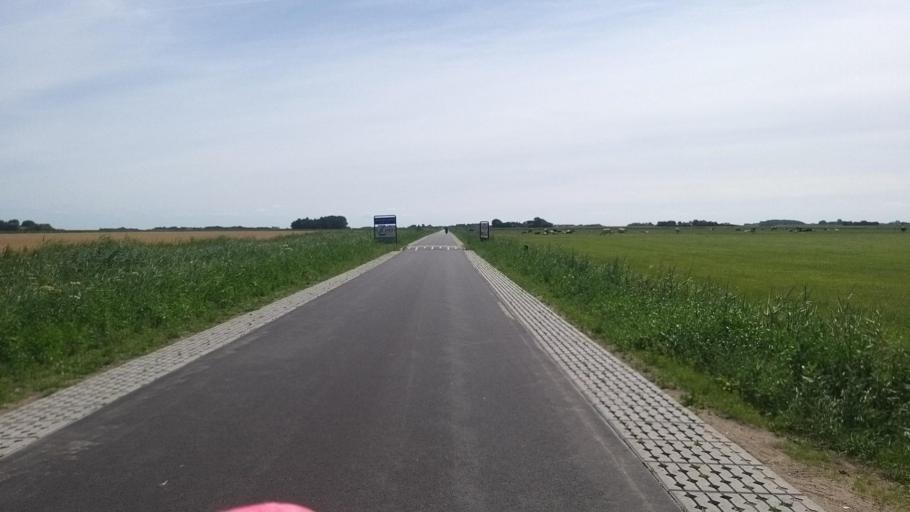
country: NL
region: North Holland
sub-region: Gemeente Texel
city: Den Burg
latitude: 53.1104
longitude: 4.8236
